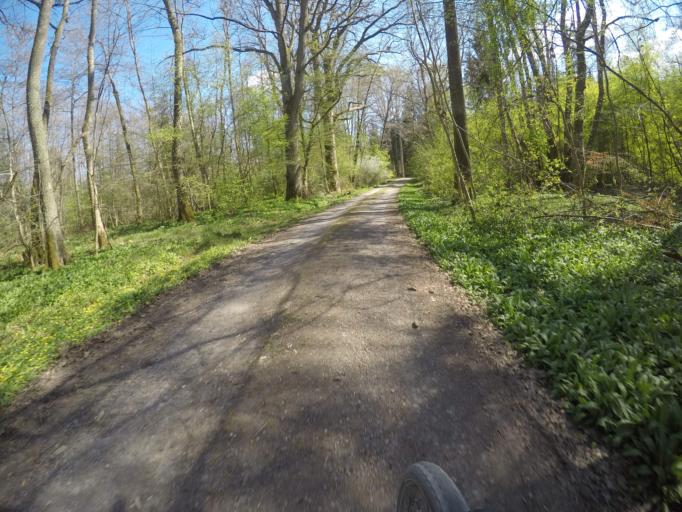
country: DE
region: Baden-Wuerttemberg
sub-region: Regierungsbezirk Stuttgart
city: Altdorf
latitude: 48.6067
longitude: 9.0174
